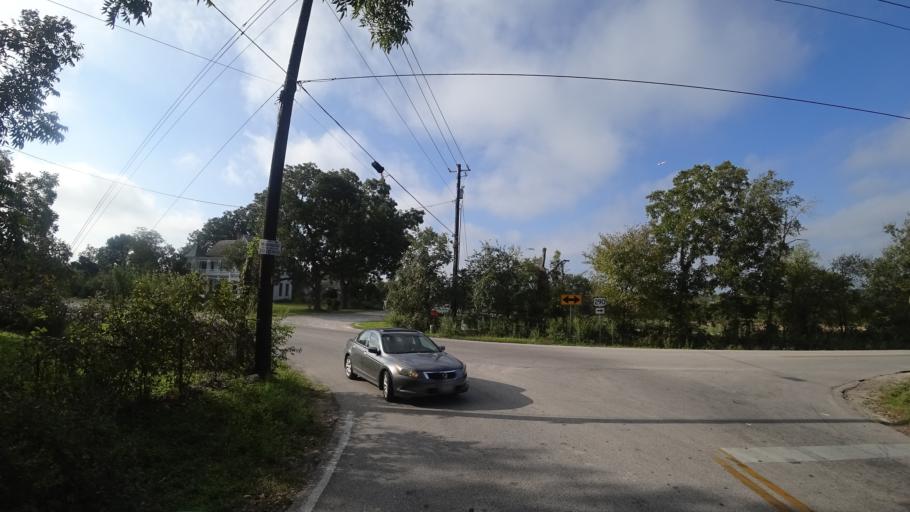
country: US
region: Texas
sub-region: Travis County
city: Pflugerville
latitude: 30.3524
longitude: -97.6475
